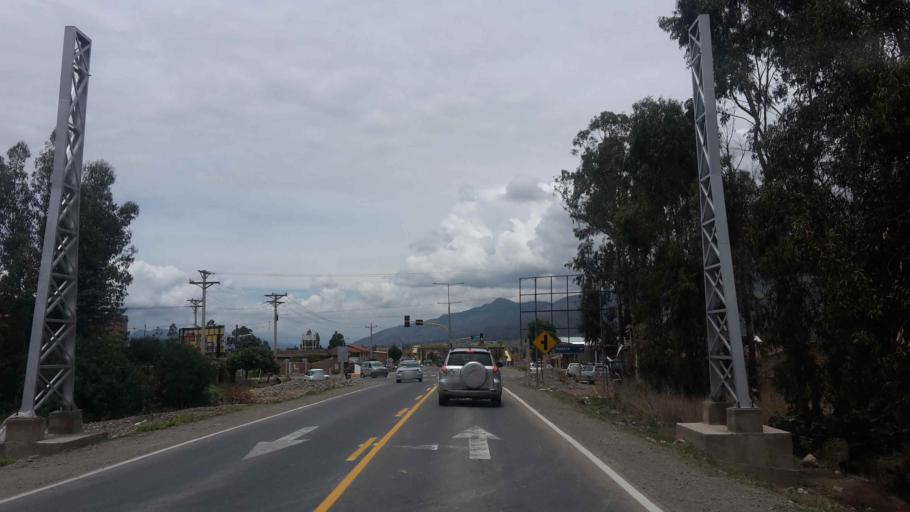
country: BO
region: Cochabamba
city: Punata
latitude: -17.5147
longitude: -65.8314
